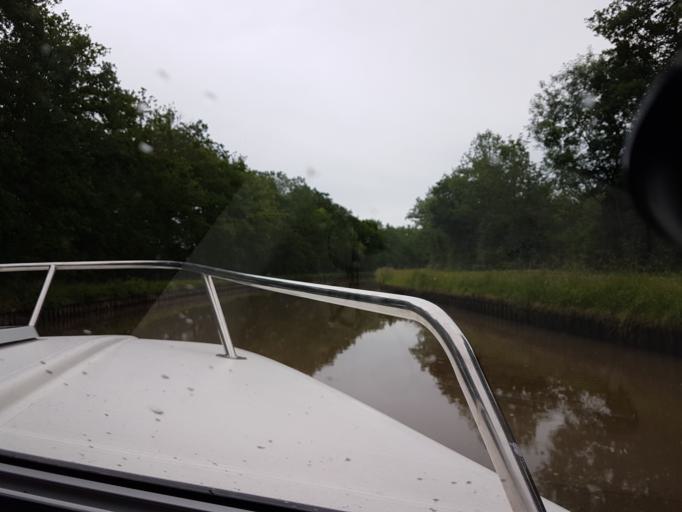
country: FR
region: Bourgogne
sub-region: Departement de la Nievre
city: Clamecy
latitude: 47.3715
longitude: 3.6086
